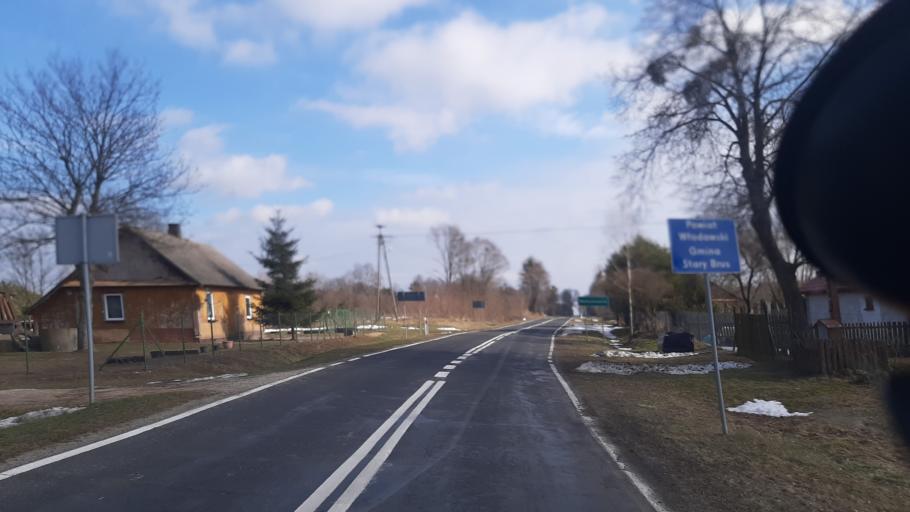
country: PL
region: Lublin Voivodeship
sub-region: Powiat wlodawski
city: Urszulin
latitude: 51.4980
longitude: 23.2084
